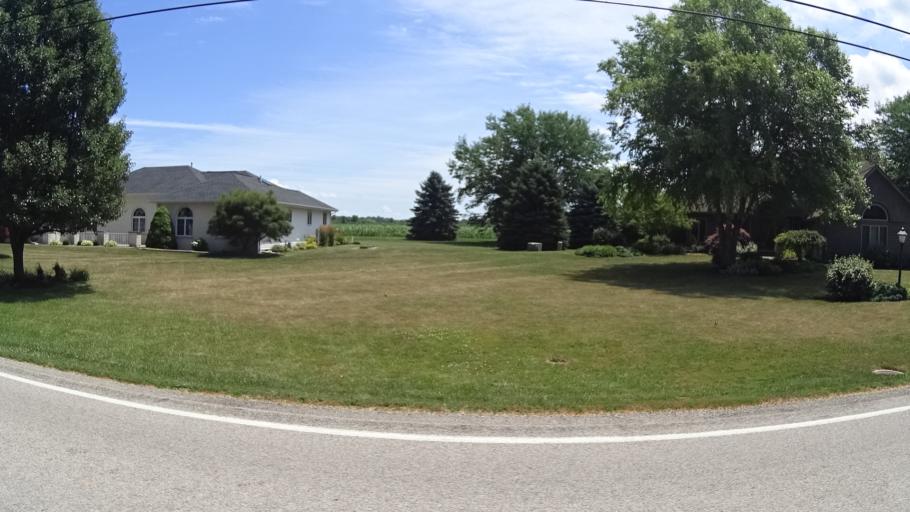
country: US
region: Ohio
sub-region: Erie County
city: Sandusky
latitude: 41.3891
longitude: -82.6621
